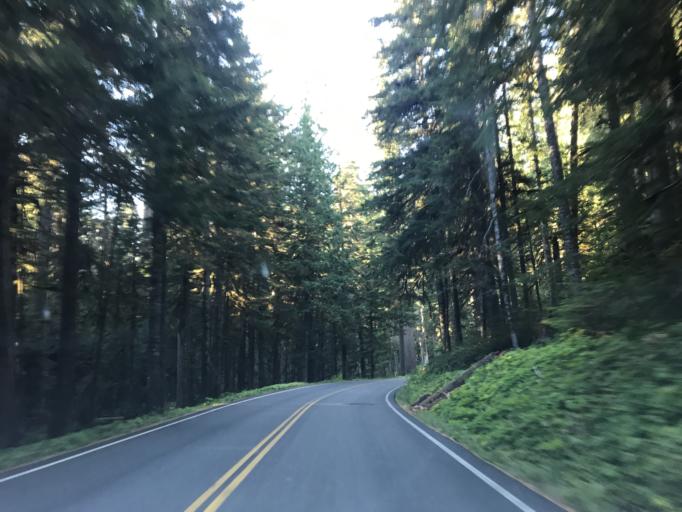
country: US
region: Washington
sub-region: Pierce County
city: Eatonville
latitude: 46.7324
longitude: -121.8382
